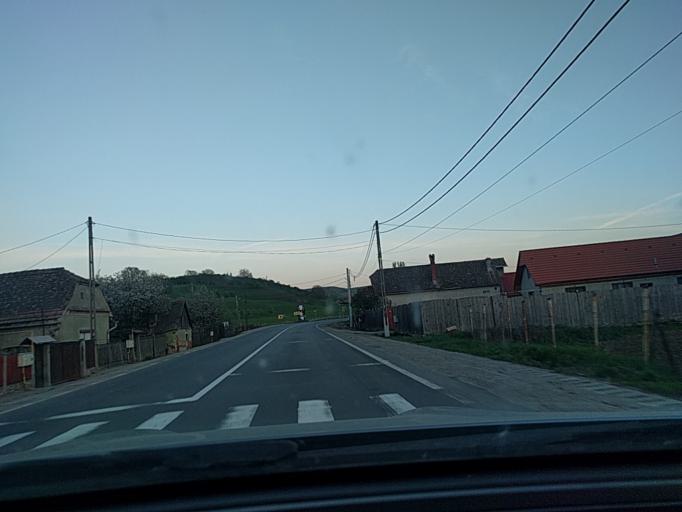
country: RO
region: Mures
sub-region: Comuna Nades
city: Nades
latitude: 46.3193
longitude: 24.7216
